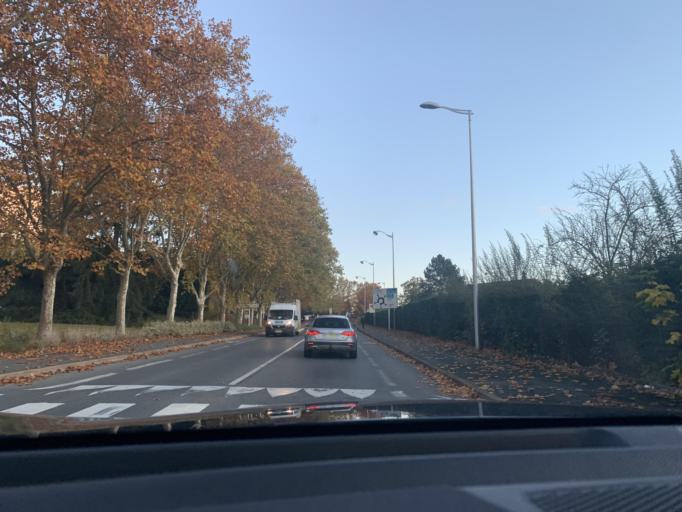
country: FR
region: Rhone-Alpes
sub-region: Departement du Rhone
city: Limas
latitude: 45.9811
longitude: 4.6967
